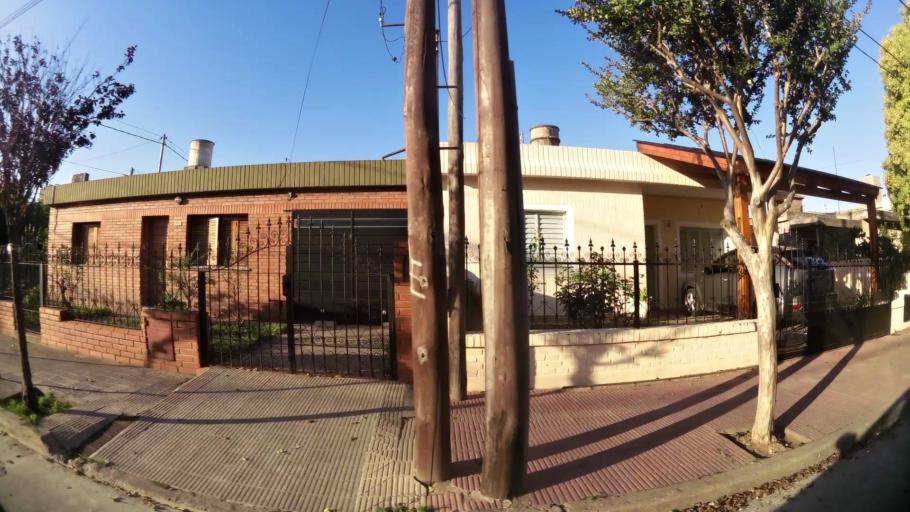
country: AR
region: Cordoba
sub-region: Departamento de Capital
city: Cordoba
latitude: -31.3711
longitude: -64.2099
